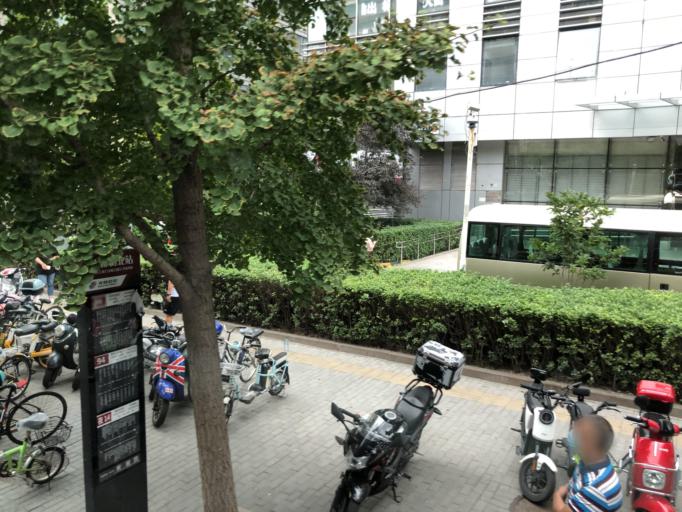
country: CN
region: Beijing
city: Jinrongjie
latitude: 39.9528
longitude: 116.3286
